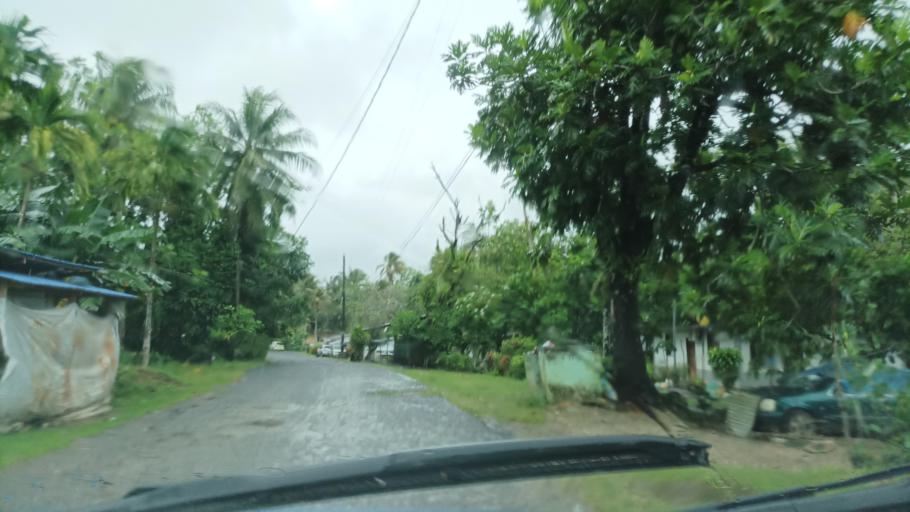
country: FM
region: Pohnpei
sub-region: Kolonia Municipality
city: Kolonia
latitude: 6.9709
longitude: 158.2078
